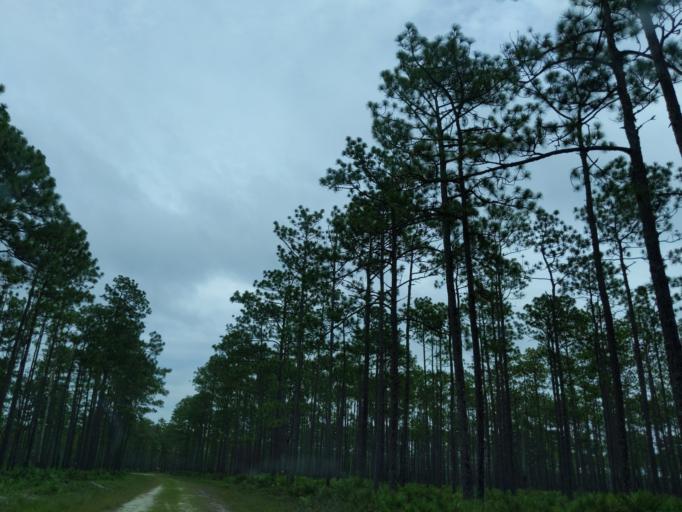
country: US
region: Florida
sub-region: Gadsden County
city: Midway
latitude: 30.3628
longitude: -84.4830
